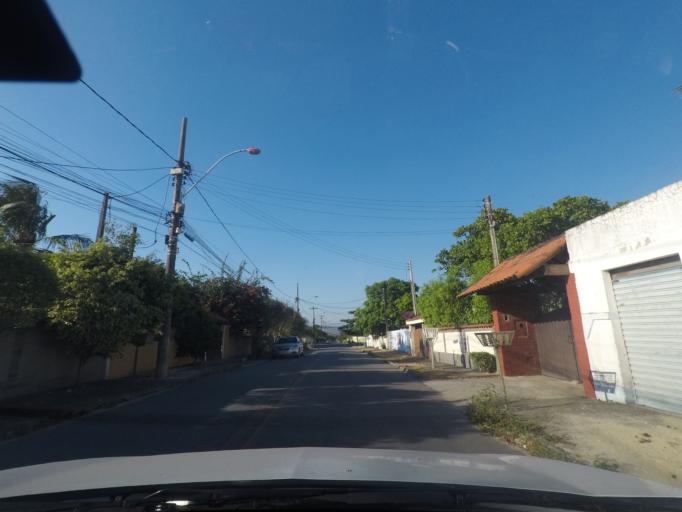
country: BR
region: Rio de Janeiro
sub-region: Marica
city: Marica
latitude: -22.9679
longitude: -42.9388
